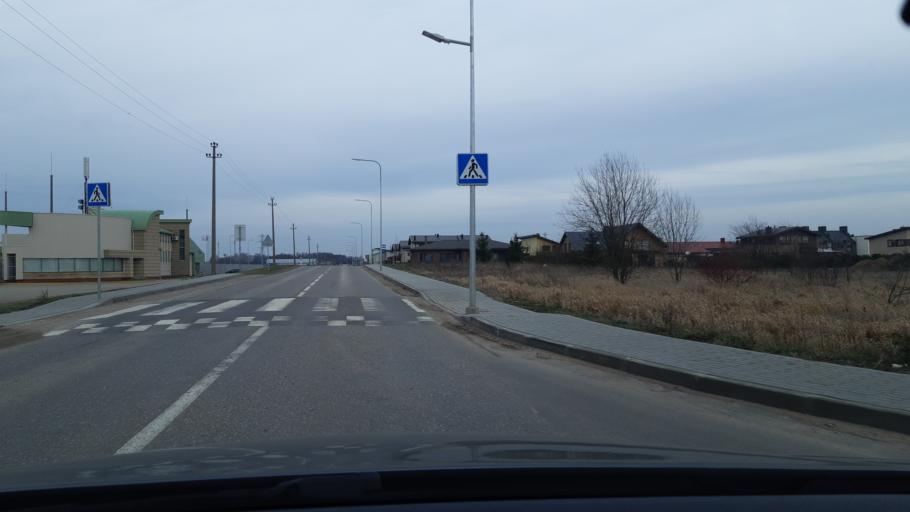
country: LT
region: Kauno apskritis
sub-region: Kaunas
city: Sargenai
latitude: 54.9509
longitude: 23.8467
